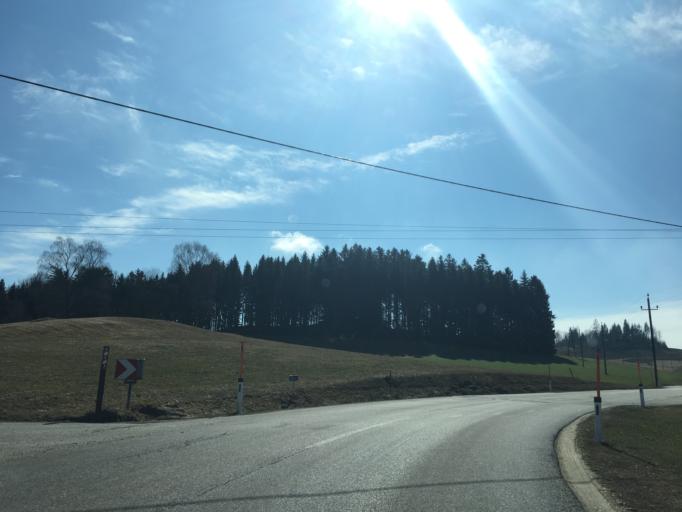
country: AT
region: Upper Austria
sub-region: Politischer Bezirk Perg
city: Sankt Georgen am Walde
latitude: 48.3289
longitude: 14.9139
